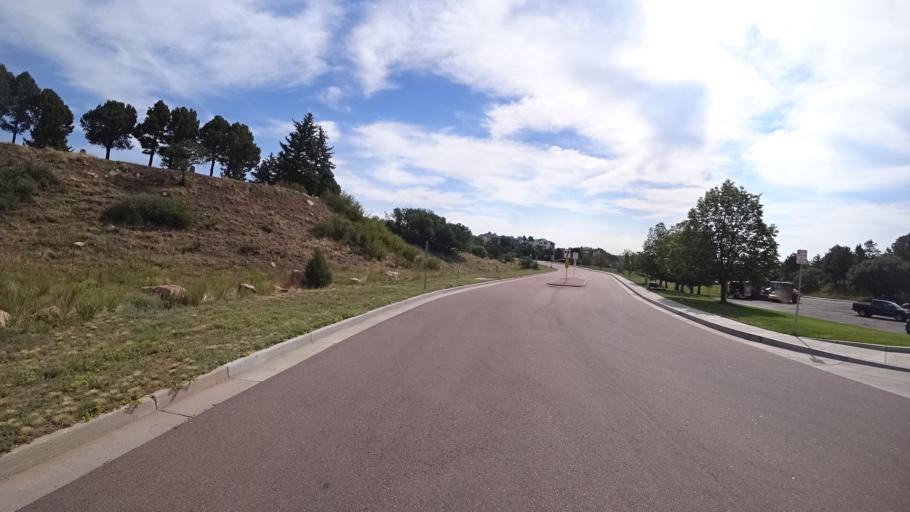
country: US
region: Colorado
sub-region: El Paso County
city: Air Force Academy
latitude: 38.9468
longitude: -104.8703
